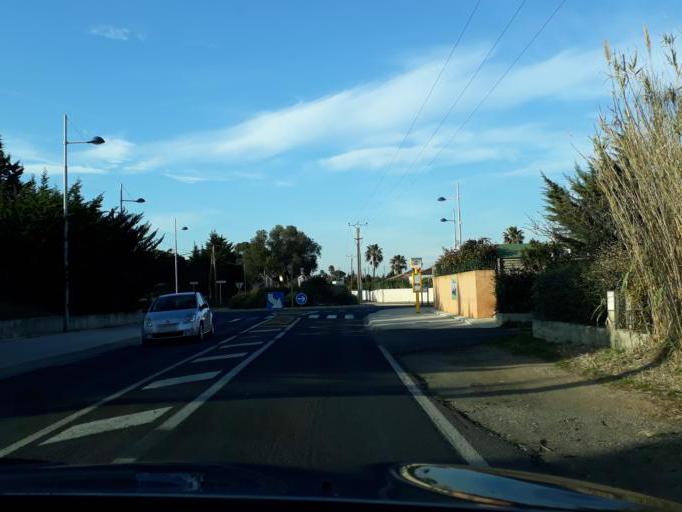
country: FR
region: Languedoc-Roussillon
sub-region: Departement de l'Herault
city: Marseillan
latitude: 43.3342
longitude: 3.5249
